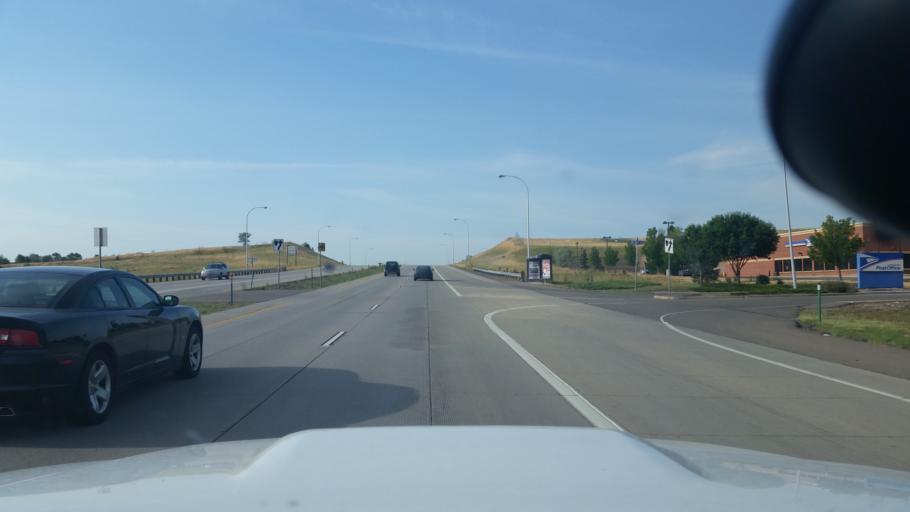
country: US
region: Colorado
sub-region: Broomfield County
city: Broomfield
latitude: 39.9038
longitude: -105.0963
